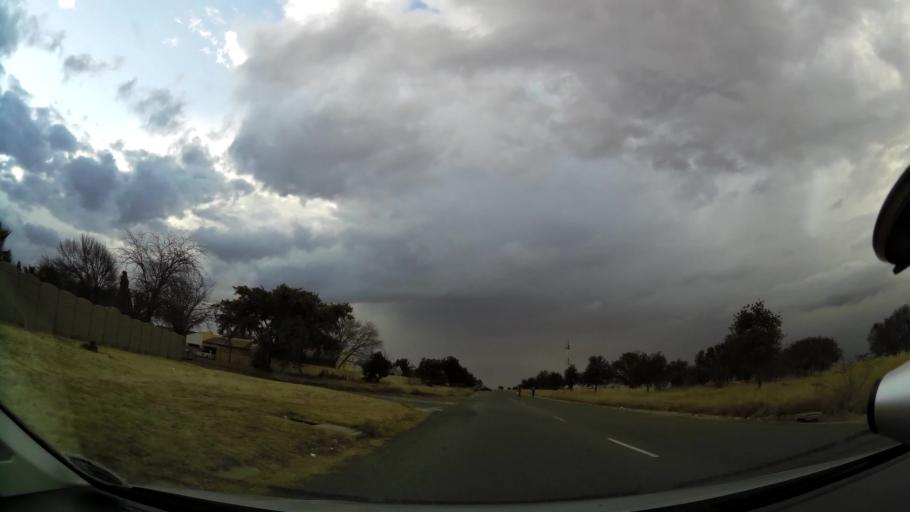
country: ZA
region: Orange Free State
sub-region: Lejweleputswa District Municipality
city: Welkom
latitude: -27.9494
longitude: 26.7348
